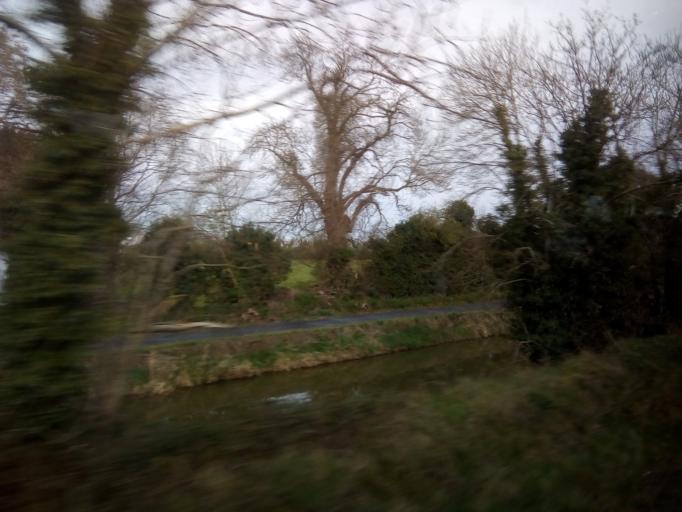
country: IE
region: Leinster
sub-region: Kildare
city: Kilcock
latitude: 53.3890
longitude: -6.6422
